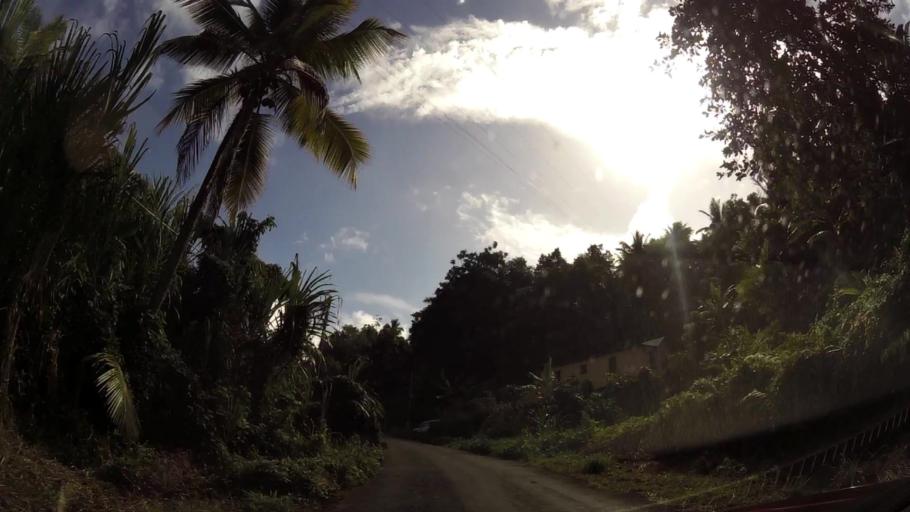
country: DM
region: Saint David
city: Castle Bruce
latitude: 15.4728
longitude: -61.2495
